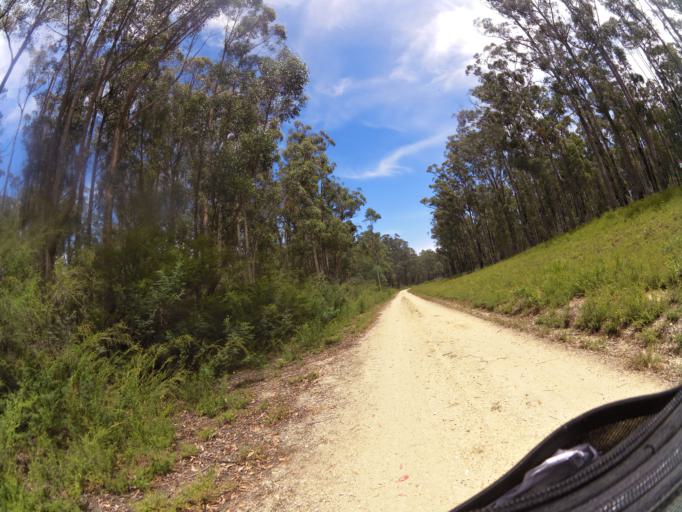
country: AU
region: Victoria
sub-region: East Gippsland
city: Lakes Entrance
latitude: -37.7442
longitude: 148.0388
